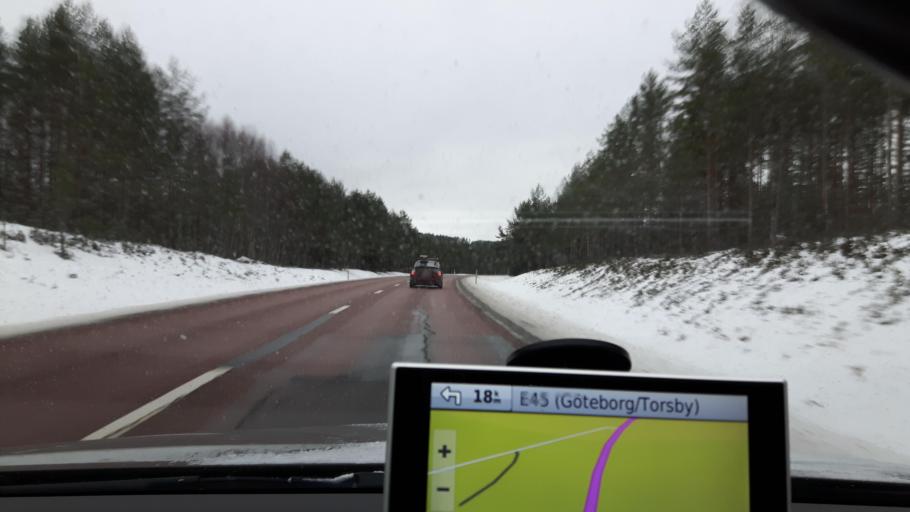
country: SE
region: Vaermland
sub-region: Hagfors Kommun
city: Ekshaerad
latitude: 60.3901
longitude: 13.2608
